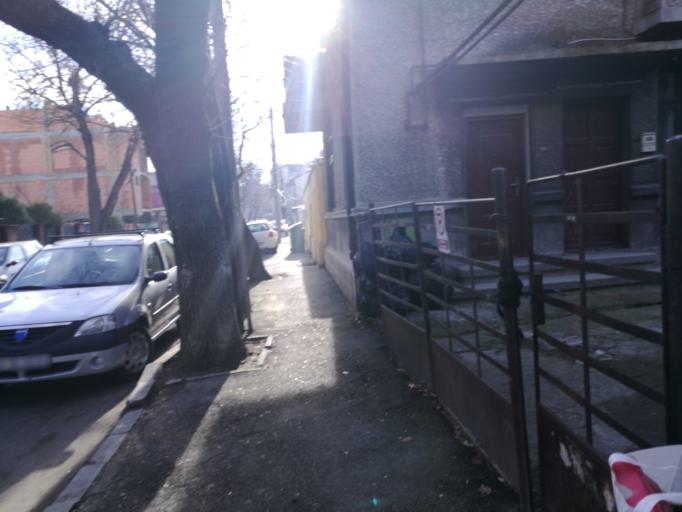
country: RO
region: Bucuresti
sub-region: Municipiul Bucuresti
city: Bucharest
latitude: 44.4360
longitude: 26.1336
